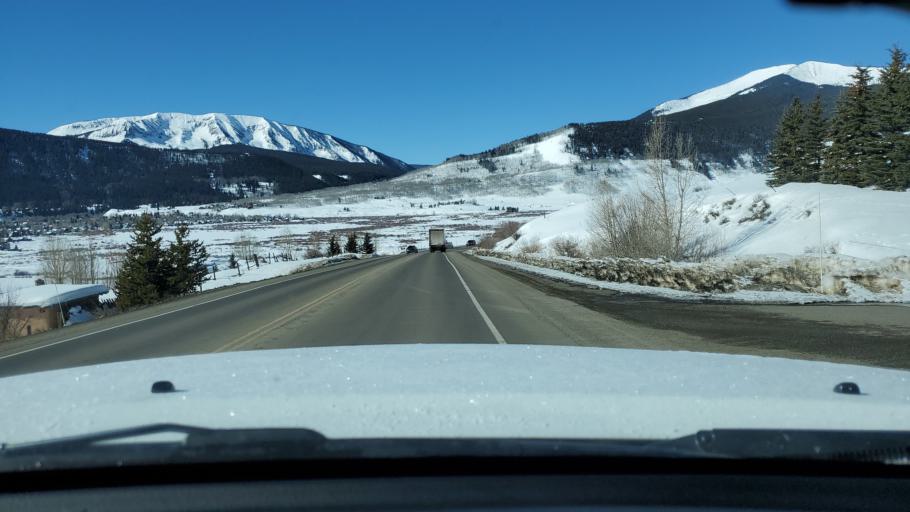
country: US
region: Colorado
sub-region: Gunnison County
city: Crested Butte
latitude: 38.8835
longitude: -106.9727
